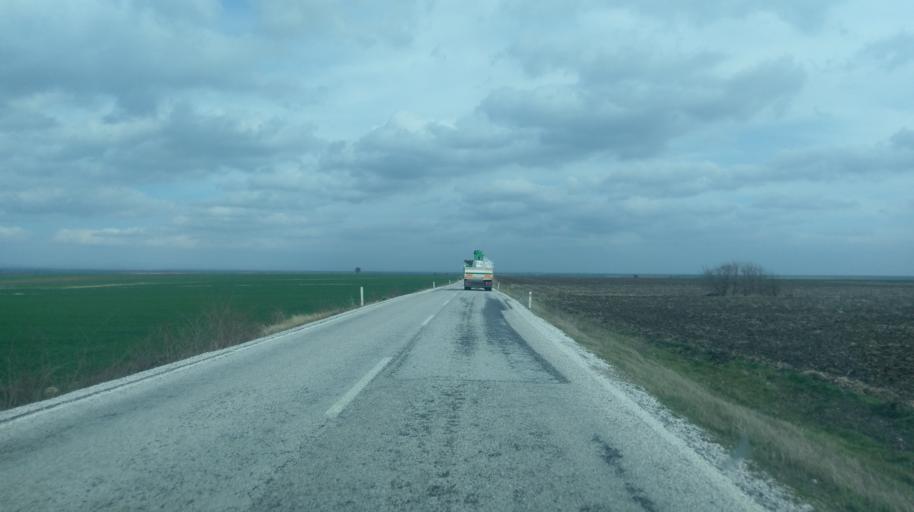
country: TR
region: Edirne
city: Haskoy
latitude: 41.6541
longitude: 26.9037
